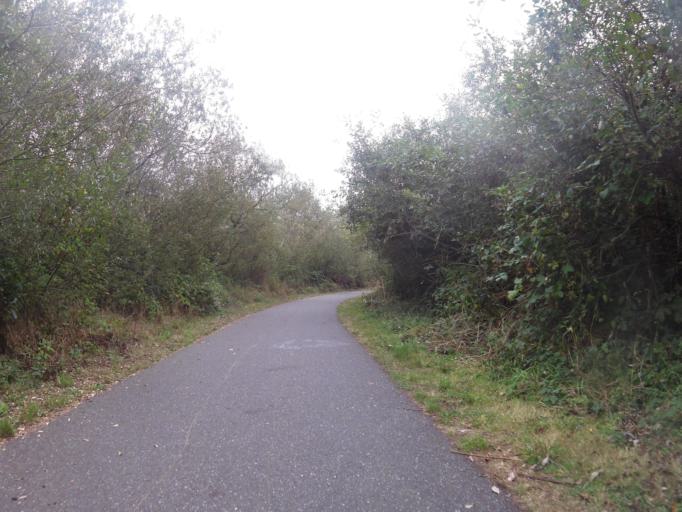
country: US
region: California
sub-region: Humboldt County
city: Bayview
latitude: 40.7664
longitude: -124.1965
